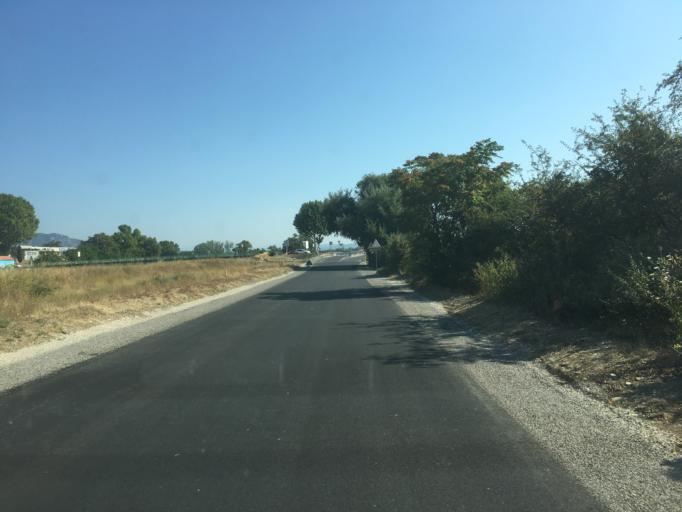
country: FR
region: Provence-Alpes-Cote d'Azur
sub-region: Departement des Alpes-de-Haute-Provence
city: Manosque
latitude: 43.8155
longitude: 5.7983
